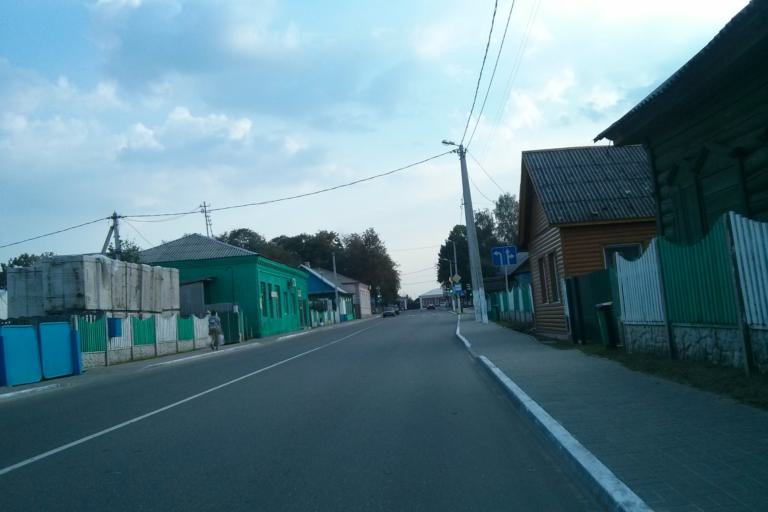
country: BY
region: Minsk
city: Chervyen'
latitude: 53.7161
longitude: 28.4170
